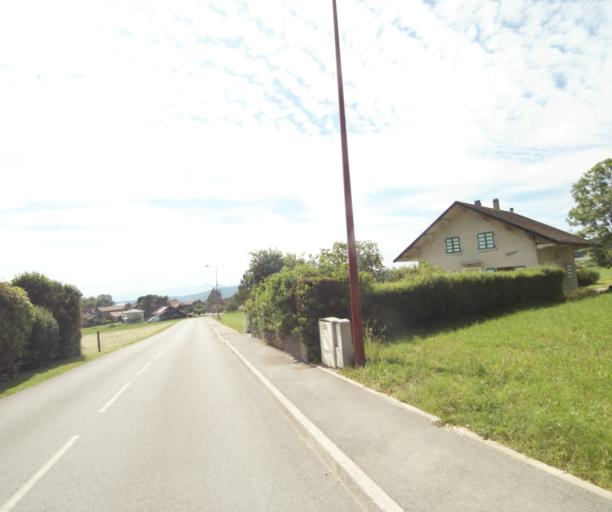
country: FR
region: Rhone-Alpes
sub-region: Departement de la Haute-Savoie
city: Perrignier
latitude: 46.3059
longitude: 6.4631
